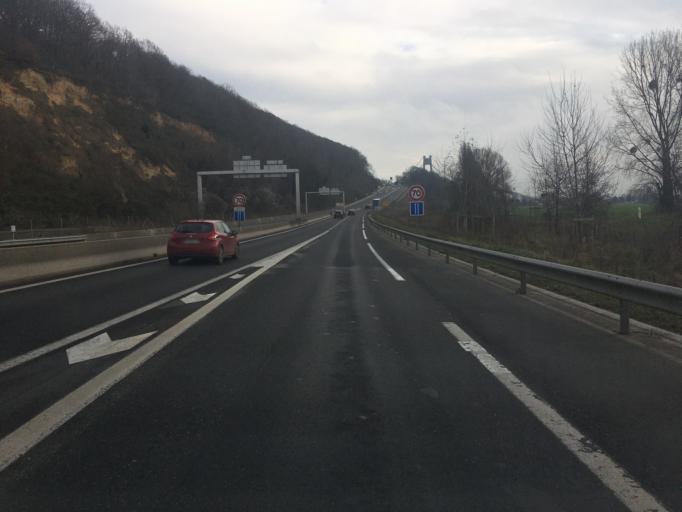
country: FR
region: Haute-Normandie
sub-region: Departement de la Seine-Maritime
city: Tancarville
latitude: 49.4821
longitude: 0.4457
